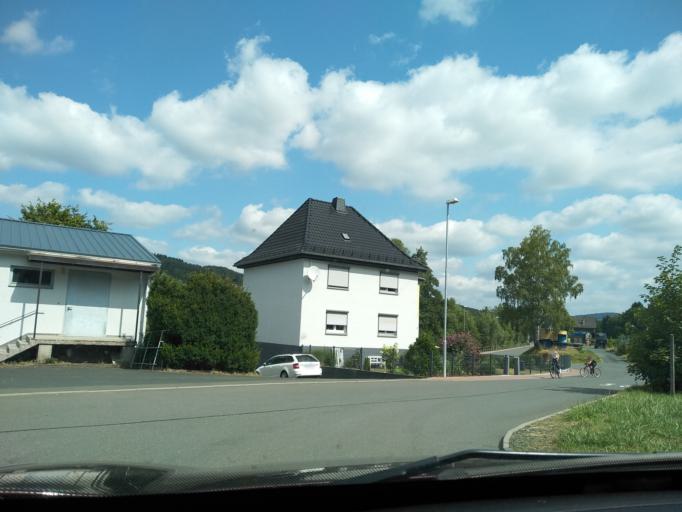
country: DE
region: Hesse
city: Dillenburg
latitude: 50.7869
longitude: 8.3265
